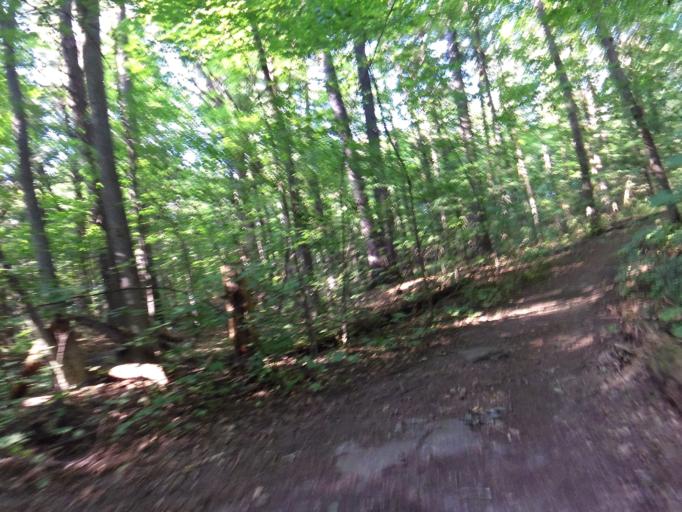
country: CA
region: Ontario
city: Ottawa
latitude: 45.4296
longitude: -75.7514
